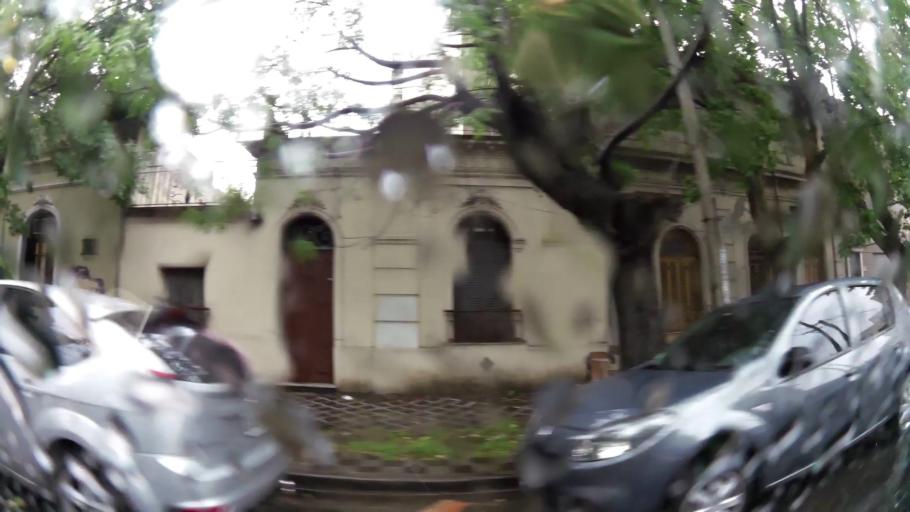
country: AR
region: Buenos Aires
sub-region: Partido de Lanus
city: Lanus
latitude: -34.7111
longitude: -58.3946
